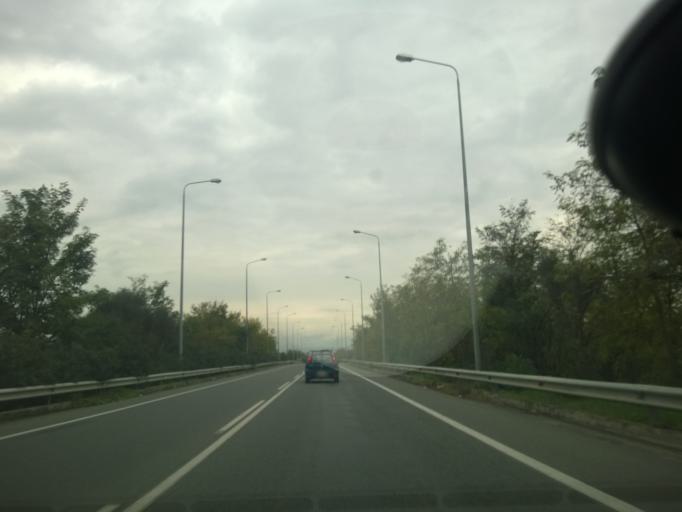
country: GR
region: Central Macedonia
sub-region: Nomos Pellis
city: Kali
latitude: 40.7968
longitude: 22.1825
